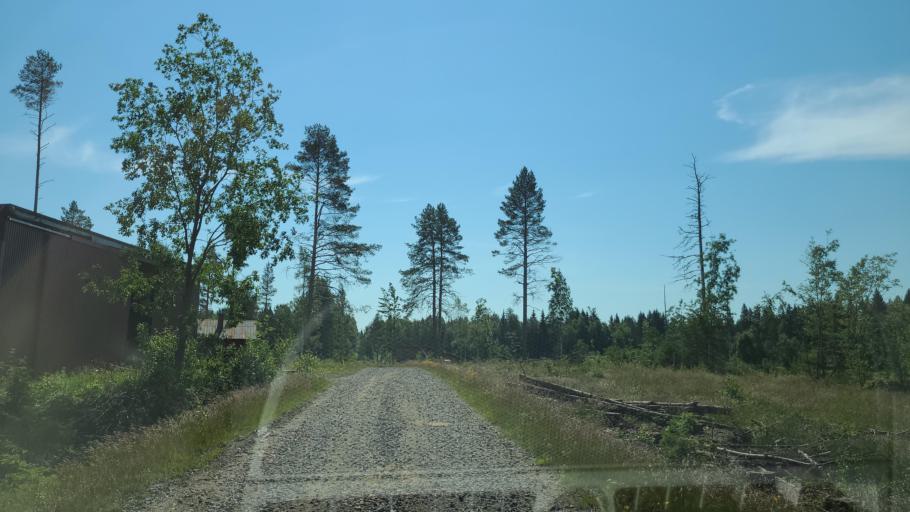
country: SE
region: Vaesterbotten
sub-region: Robertsfors Kommun
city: Robertsfors
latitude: 64.0882
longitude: 20.8394
